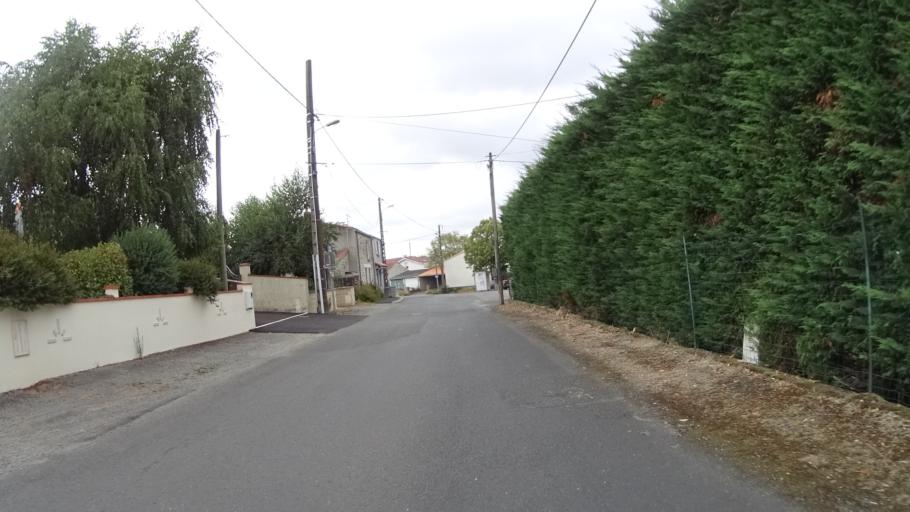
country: FR
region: Pays de la Loire
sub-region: Departement de la Loire-Atlantique
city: La Montagne
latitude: 47.1934
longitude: -1.6999
